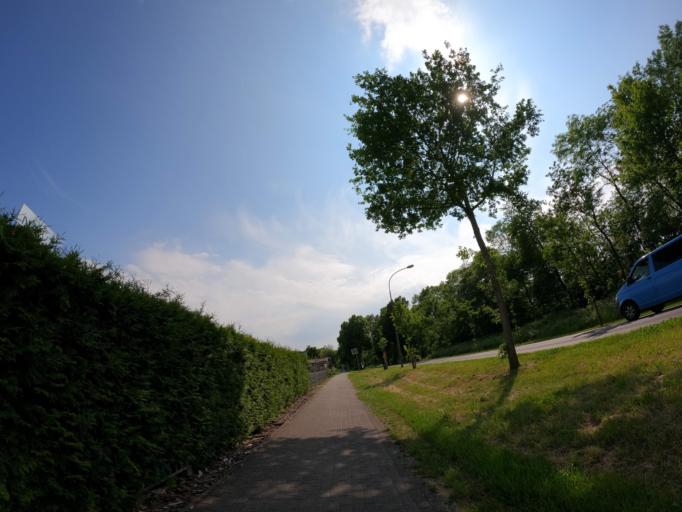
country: DE
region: Mecklenburg-Vorpommern
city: Stralsund
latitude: 54.2908
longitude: 13.0540
